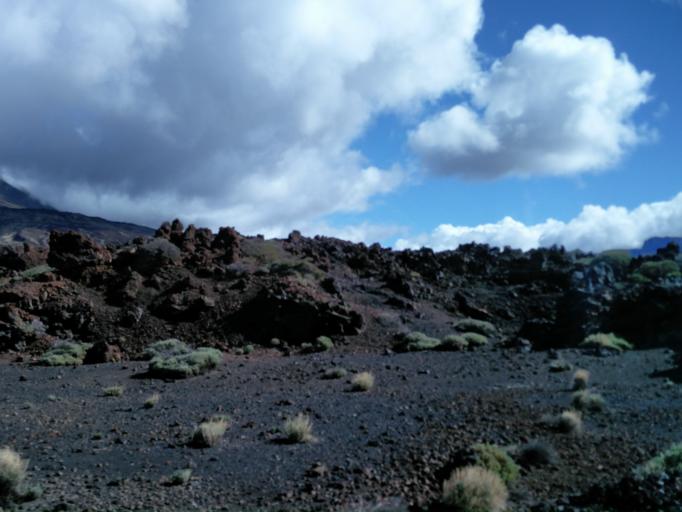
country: ES
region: Canary Islands
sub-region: Provincia de Santa Cruz de Tenerife
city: Vilaflor
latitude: 28.2149
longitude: -16.6668
